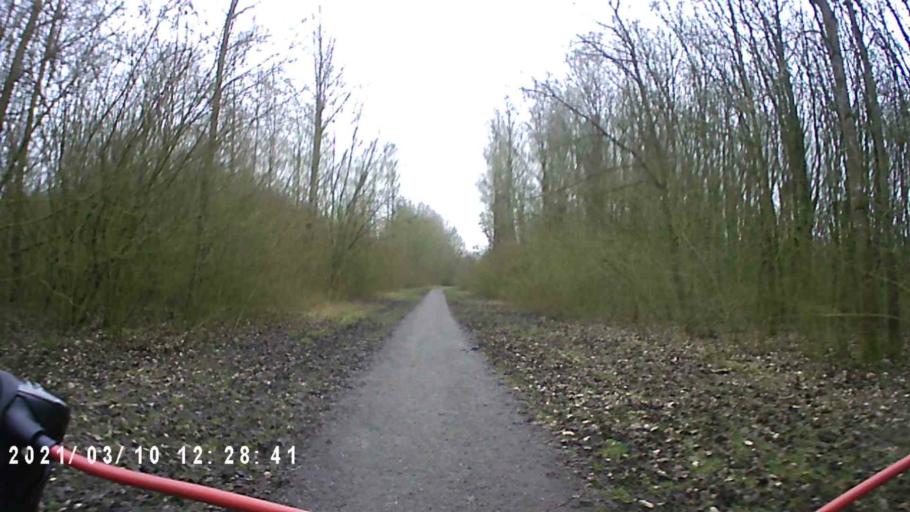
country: NL
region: Groningen
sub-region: Gemeente Groningen
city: Oosterpark
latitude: 53.2521
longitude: 6.6157
